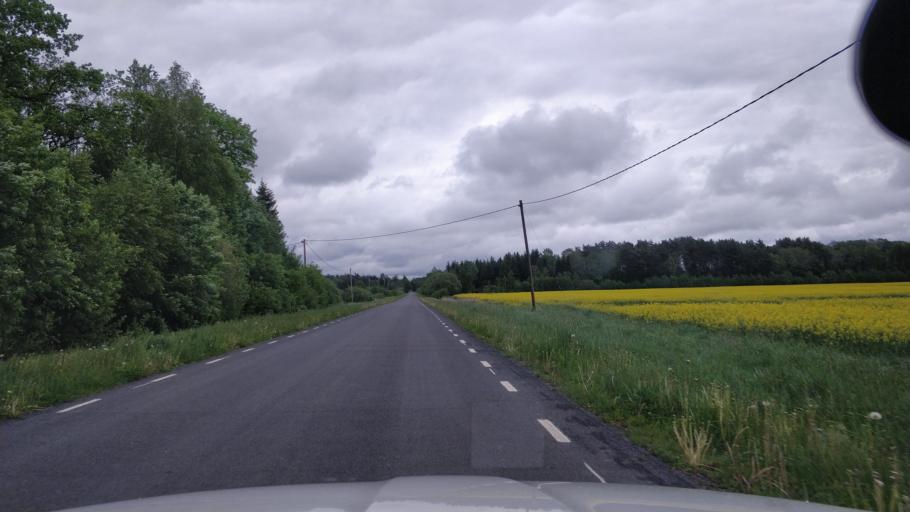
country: EE
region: Raplamaa
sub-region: Maerjamaa vald
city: Marjamaa
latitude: 58.7566
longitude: 24.2399
